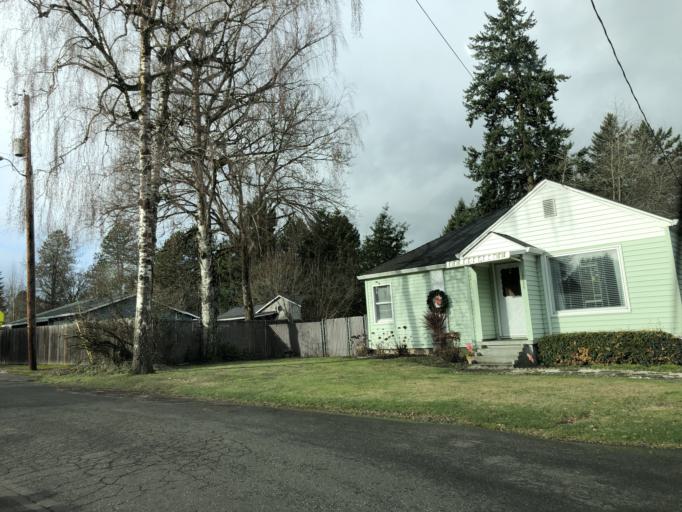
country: US
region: Oregon
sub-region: Washington County
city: Tigard
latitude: 45.4258
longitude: -122.7831
